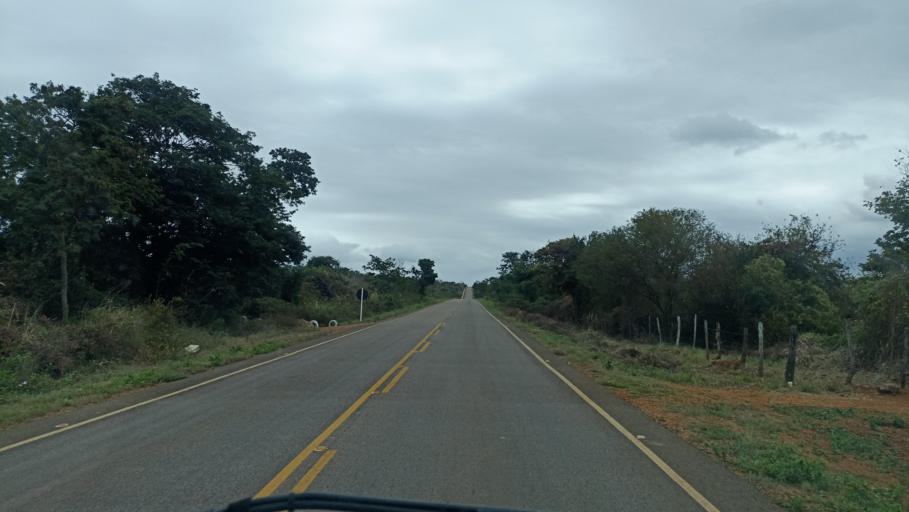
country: BR
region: Bahia
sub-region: Andarai
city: Vera Cruz
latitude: -13.0019
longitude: -40.9893
